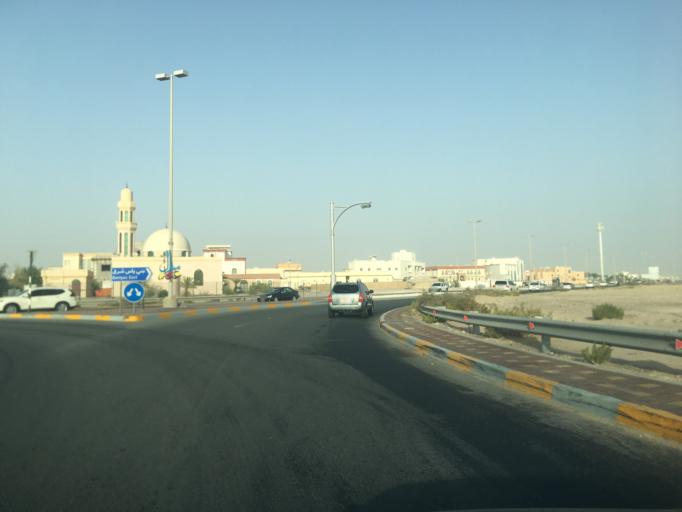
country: AE
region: Abu Dhabi
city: Abu Dhabi
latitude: 24.3225
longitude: 54.6273
